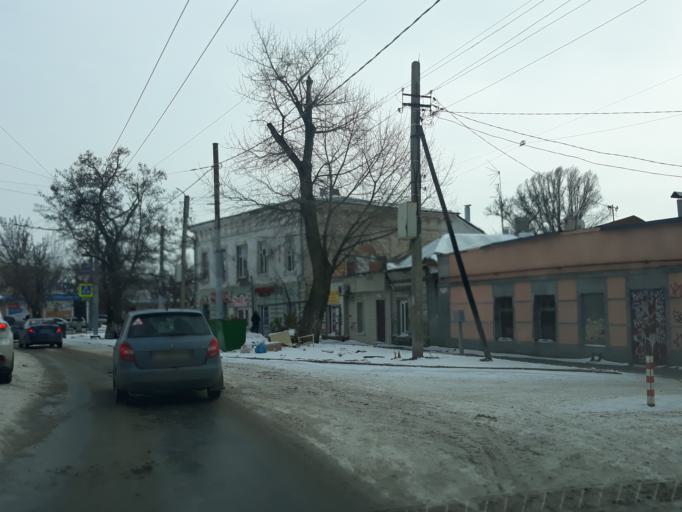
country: RU
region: Rostov
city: Taganrog
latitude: 47.2122
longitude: 38.9147
